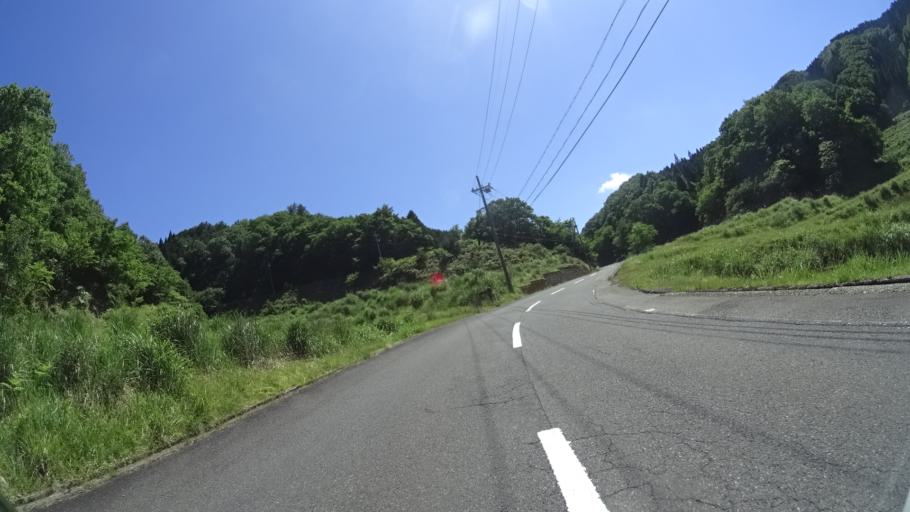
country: JP
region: Kyoto
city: Fukuchiyama
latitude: 35.4064
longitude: 135.0562
